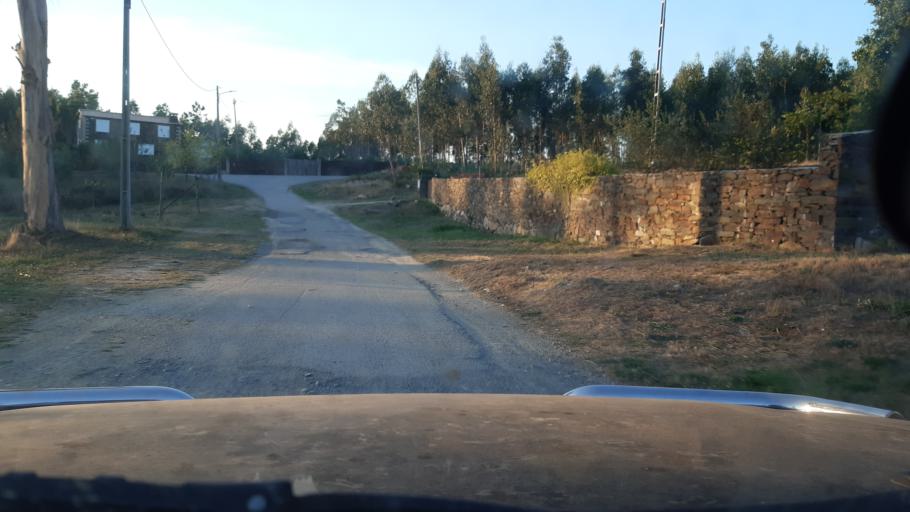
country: PT
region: Viseu
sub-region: Mortagua
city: Mortagua
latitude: 40.5459
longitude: -8.2617
